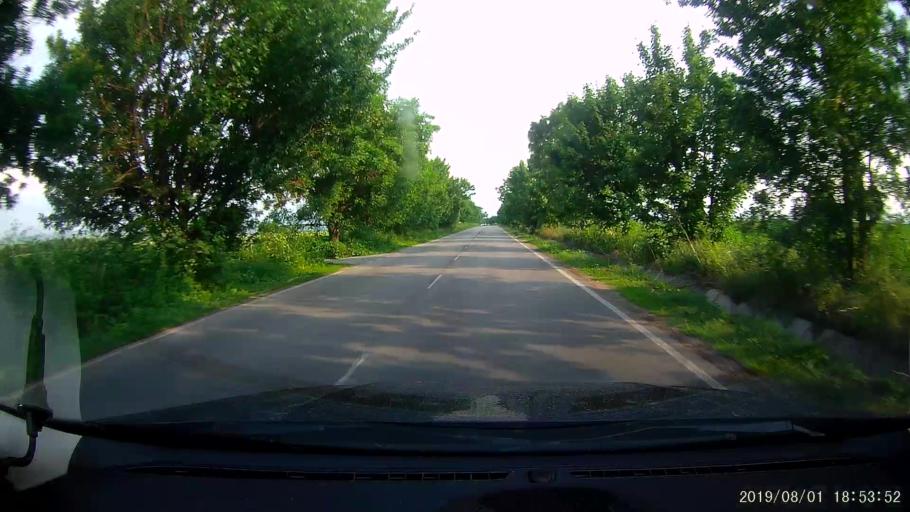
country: BG
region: Shumen
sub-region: Obshtina Shumen
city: Shumen
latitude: 43.2128
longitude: 26.9981
